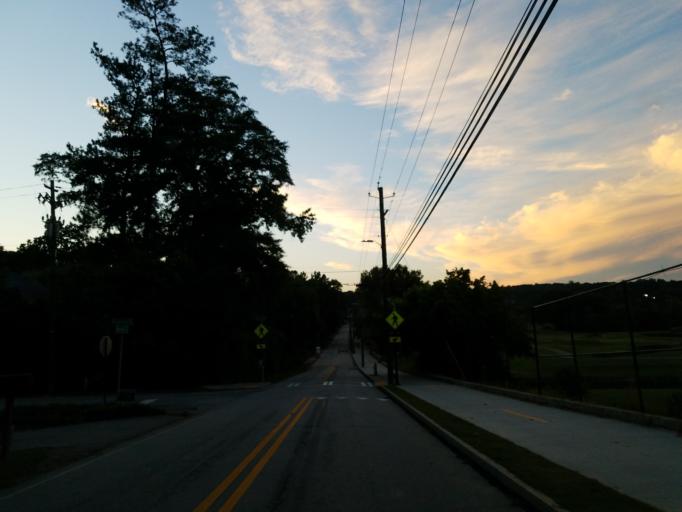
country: US
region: Georgia
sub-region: DeKalb County
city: North Atlanta
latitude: 33.8669
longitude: -84.3925
